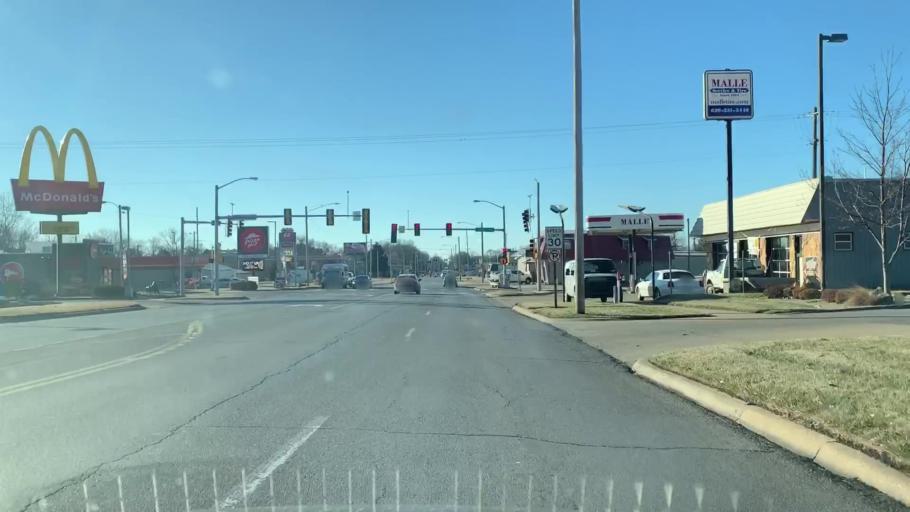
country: US
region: Kansas
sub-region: Crawford County
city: Pittsburg
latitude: 37.3970
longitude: -94.7051
